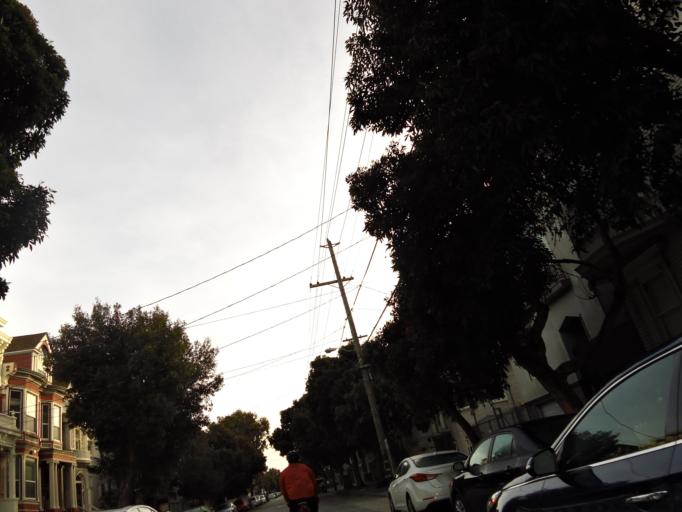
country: US
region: California
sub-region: San Francisco County
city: San Francisco
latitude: 37.7712
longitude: -122.4453
